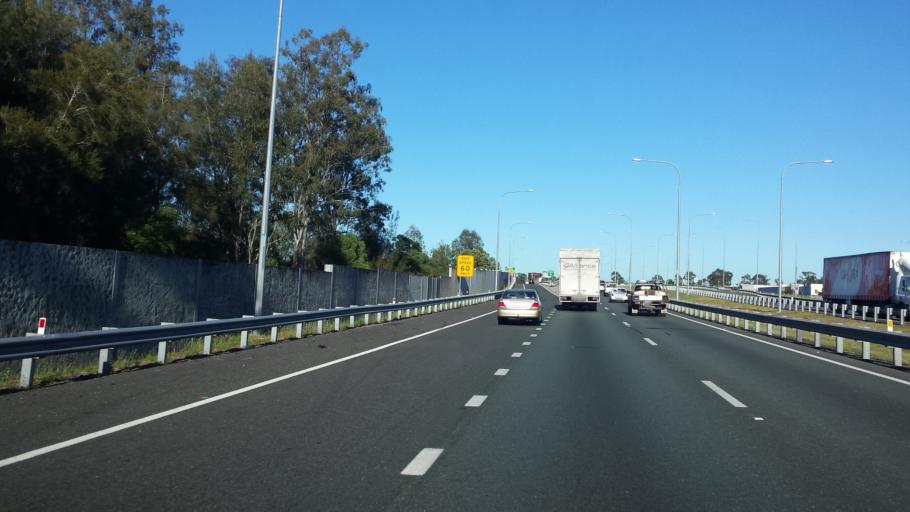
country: AU
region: Queensland
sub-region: Logan
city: Slacks Creek
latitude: -27.6661
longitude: 153.1445
